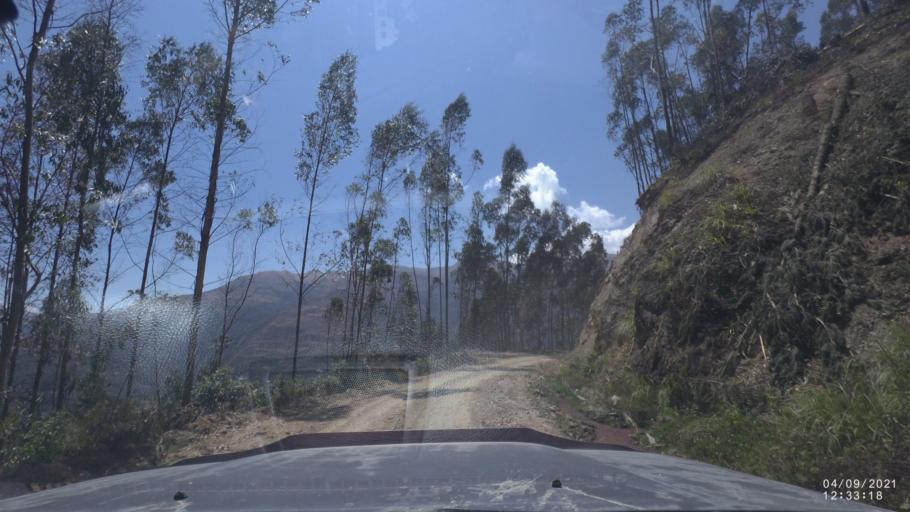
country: BO
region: Cochabamba
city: Colchani
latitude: -17.2244
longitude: -66.5188
